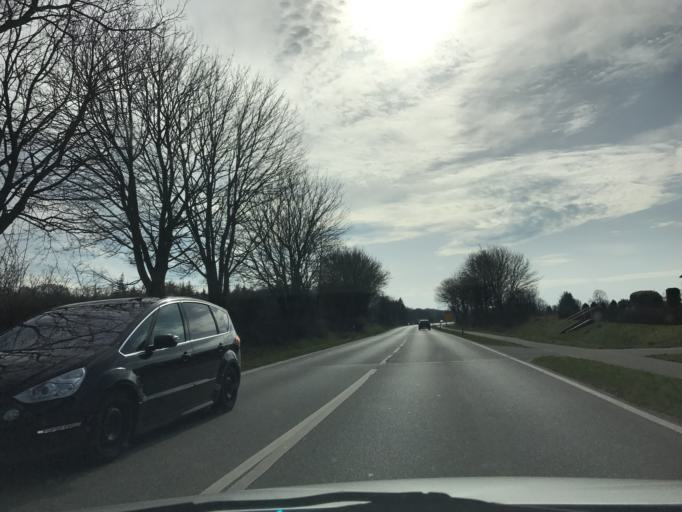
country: DE
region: Schleswig-Holstein
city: Goosefeld
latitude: 54.4398
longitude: 9.8181
